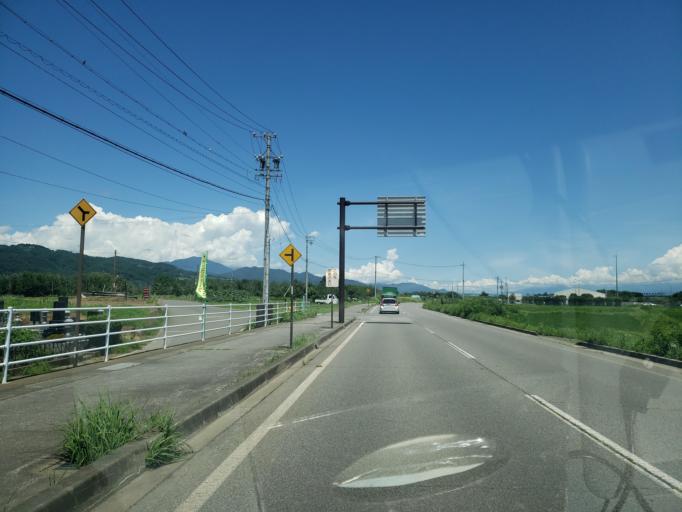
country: JP
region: Nagano
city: Nagano-shi
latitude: 36.5425
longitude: 138.1120
